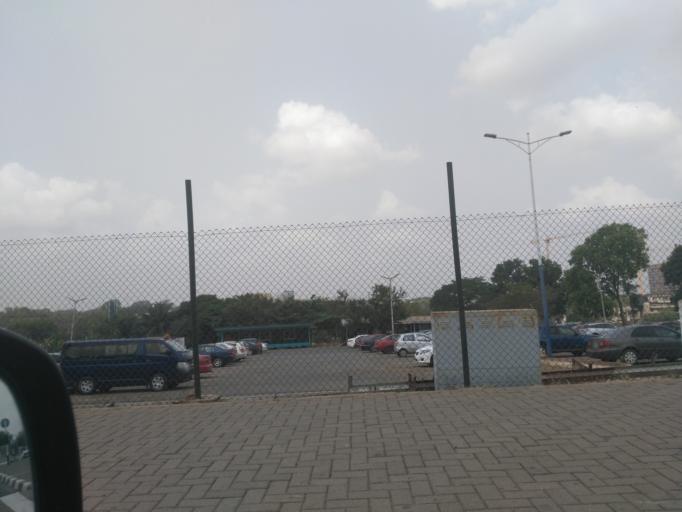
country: GH
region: Greater Accra
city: Accra
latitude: 5.6072
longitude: -0.1726
